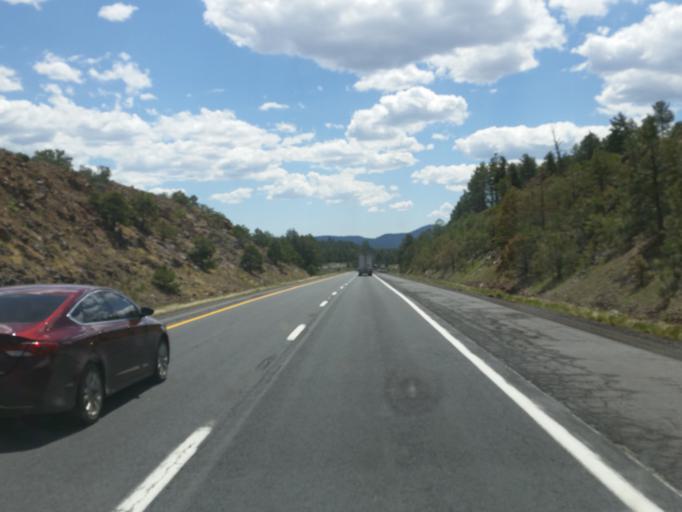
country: US
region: Arizona
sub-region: Coconino County
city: Parks
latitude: 35.2535
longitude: -112.0049
